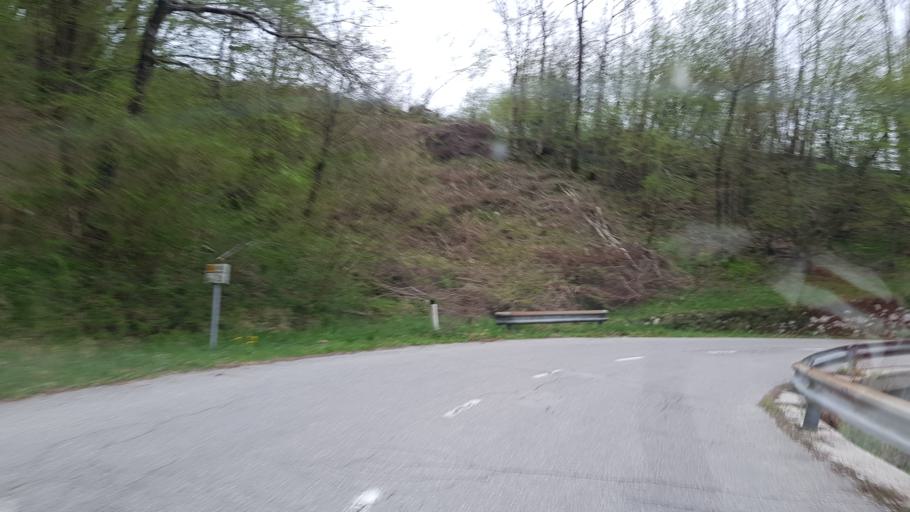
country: IT
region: Friuli Venezia Giulia
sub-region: Provincia di Udine
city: Pulfero
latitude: 46.2547
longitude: 13.4488
